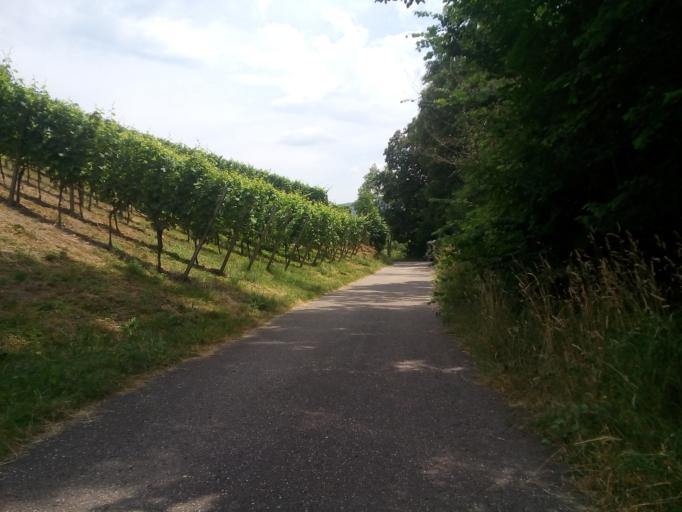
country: DE
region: Baden-Wuerttemberg
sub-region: Freiburg Region
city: Kappelrodeck
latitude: 48.6068
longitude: 8.0924
